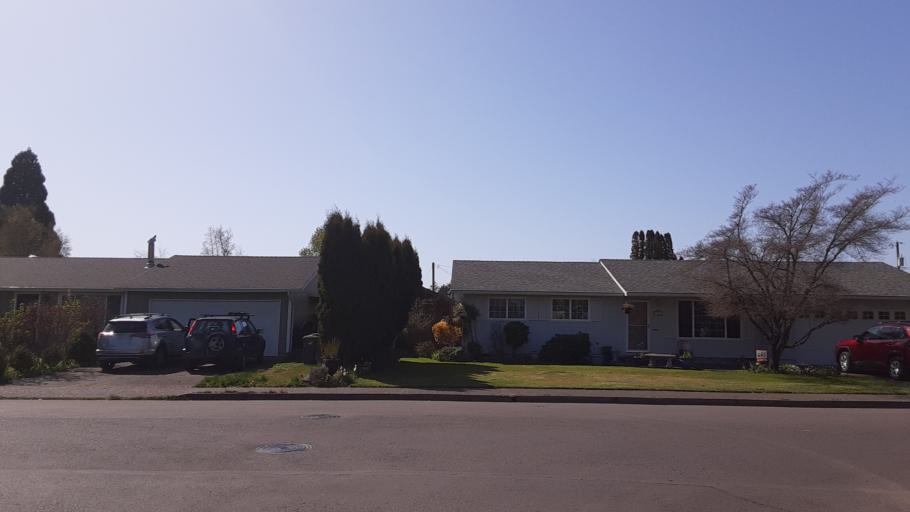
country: US
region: Oregon
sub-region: Benton County
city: Corvallis
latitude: 44.5397
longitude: -123.2603
